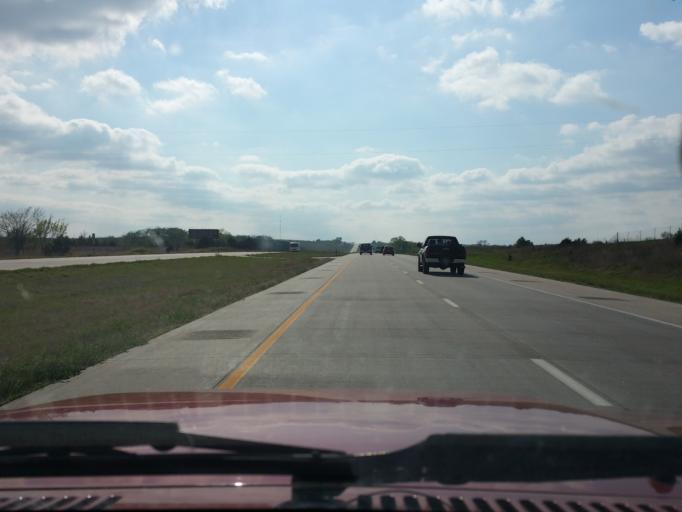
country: US
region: Kansas
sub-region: Wabaunsee County
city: Alma
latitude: 39.0656
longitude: -96.2600
